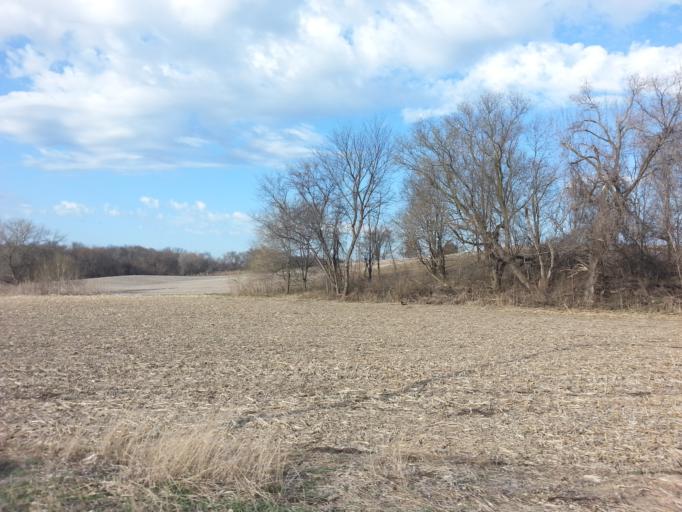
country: US
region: Minnesota
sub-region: Dakota County
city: Hastings
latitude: 44.7653
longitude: -92.8372
